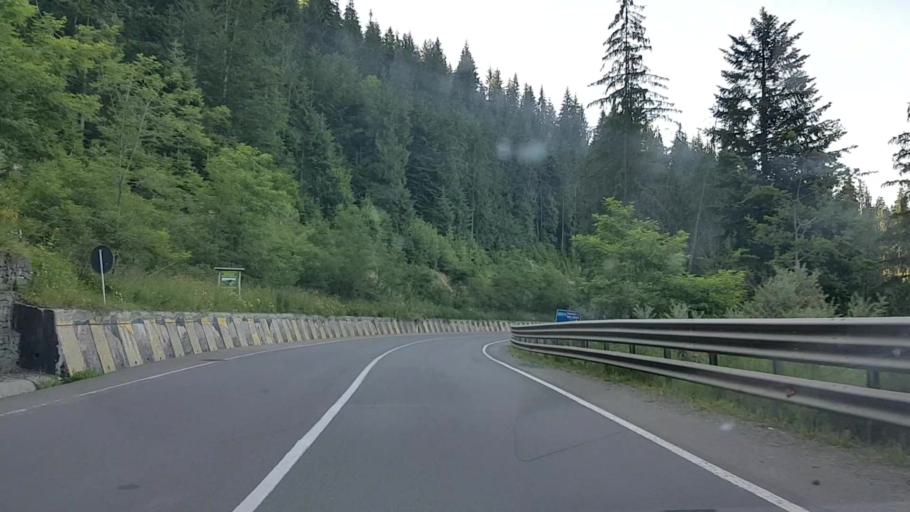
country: RO
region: Bistrita-Nasaud
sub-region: Comuna Lunca Ilvei
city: Lunca Ilvei
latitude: 47.2298
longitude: 24.9633
